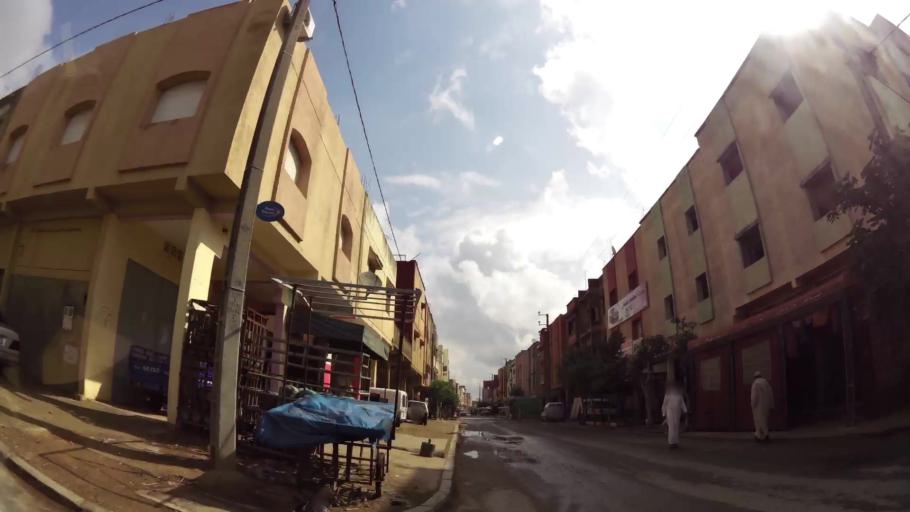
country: MA
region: Rabat-Sale-Zemmour-Zaer
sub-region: Khemisset
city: Tiflet
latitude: 33.8958
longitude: -6.3170
